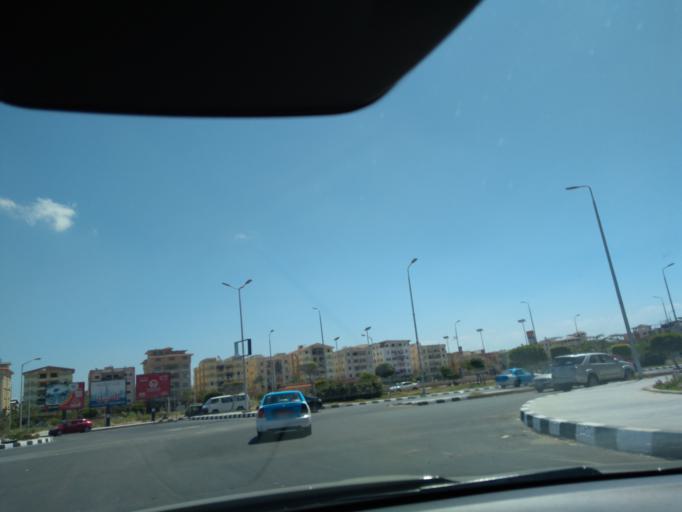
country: EG
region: Dumyat
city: Faraskur
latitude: 31.4357
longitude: 31.6746
